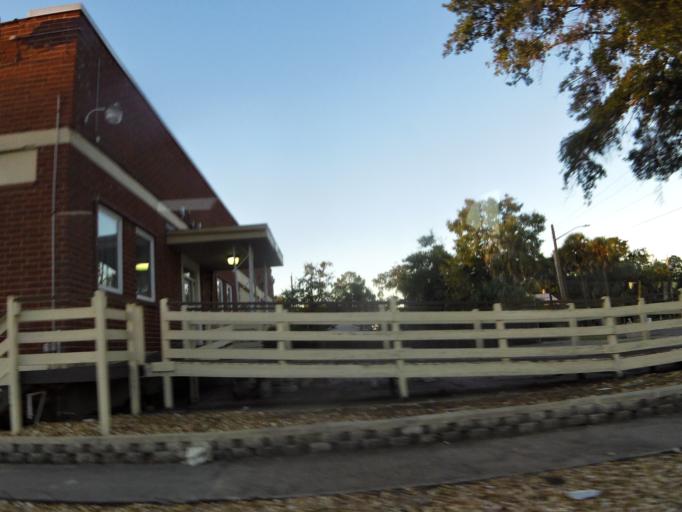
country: US
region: Florida
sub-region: Duval County
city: Jacksonville
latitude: 30.3521
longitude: -81.6524
